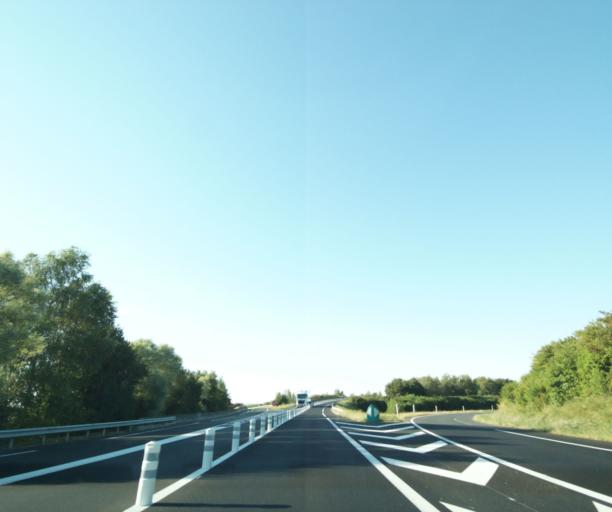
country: FR
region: Ile-de-France
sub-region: Departement de Seine-et-Marne
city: Marolles-sur-Seine
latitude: 48.3786
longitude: 3.0210
